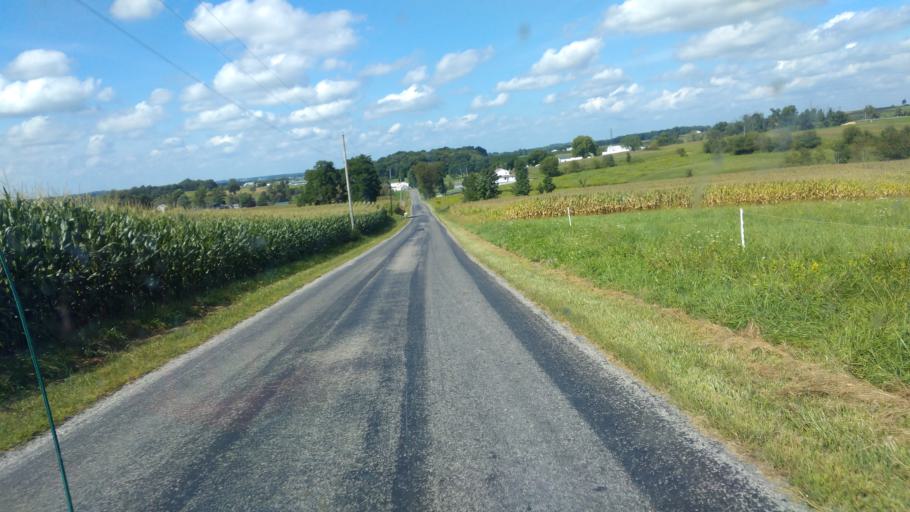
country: US
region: Ohio
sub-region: Holmes County
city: Millersburg
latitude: 40.6408
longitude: -81.8516
